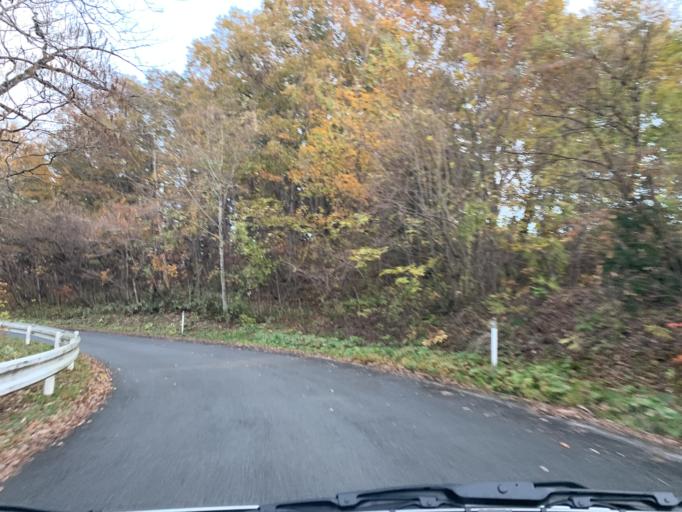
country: JP
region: Iwate
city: Ichinoseki
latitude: 38.9941
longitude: 141.0121
